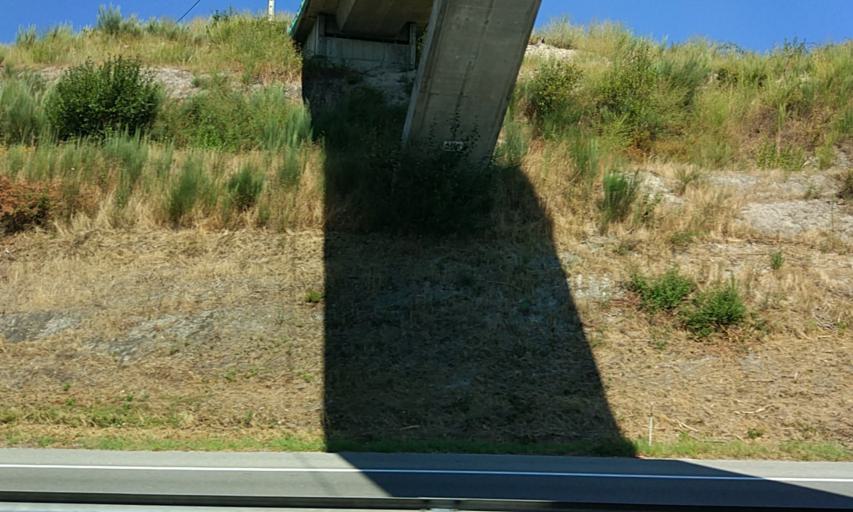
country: PT
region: Porto
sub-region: Amarante
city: Amarante
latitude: 41.2410
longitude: -8.1164
